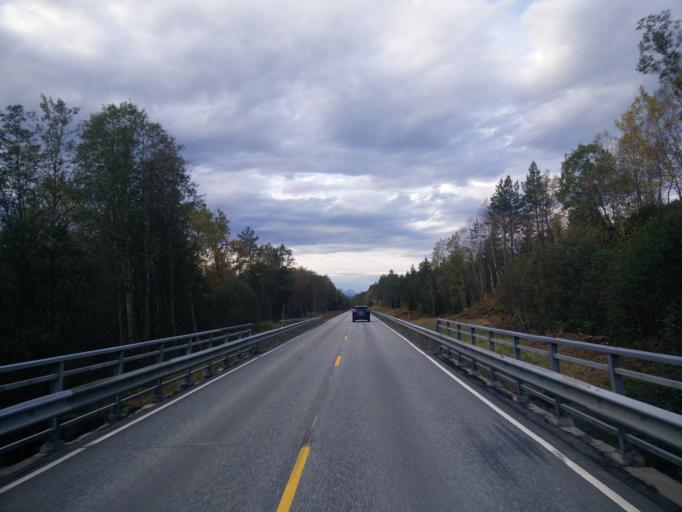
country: NO
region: More og Romsdal
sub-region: Molde
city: Hjelset
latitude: 62.7950
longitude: 7.5436
